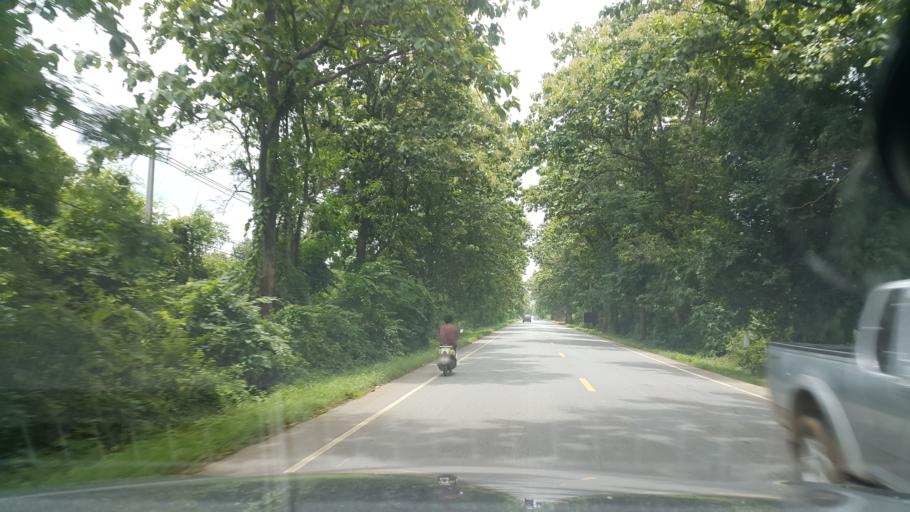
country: TH
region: Sukhothai
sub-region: Amphoe Si Satchanalai
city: Si Satchanalai
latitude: 17.5394
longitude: 99.8115
